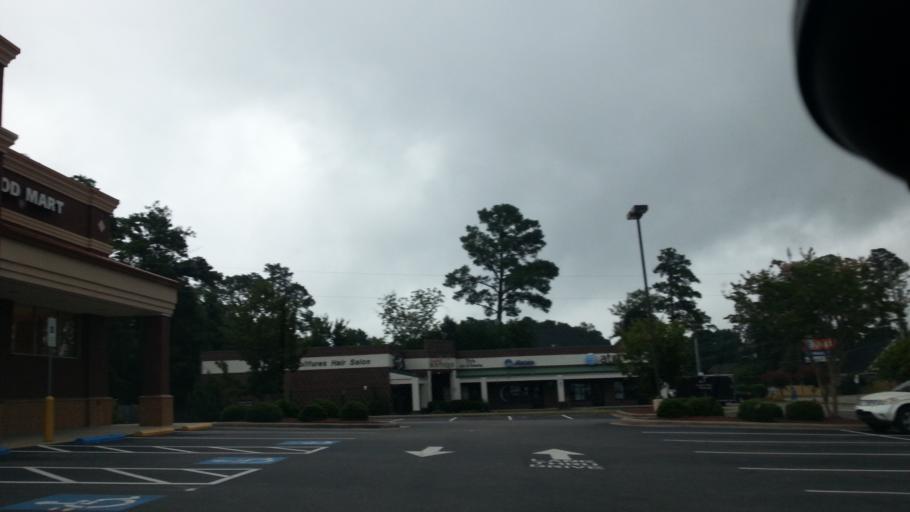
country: US
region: North Carolina
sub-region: Cumberland County
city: Fayetteville
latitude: 35.0676
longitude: -78.9503
